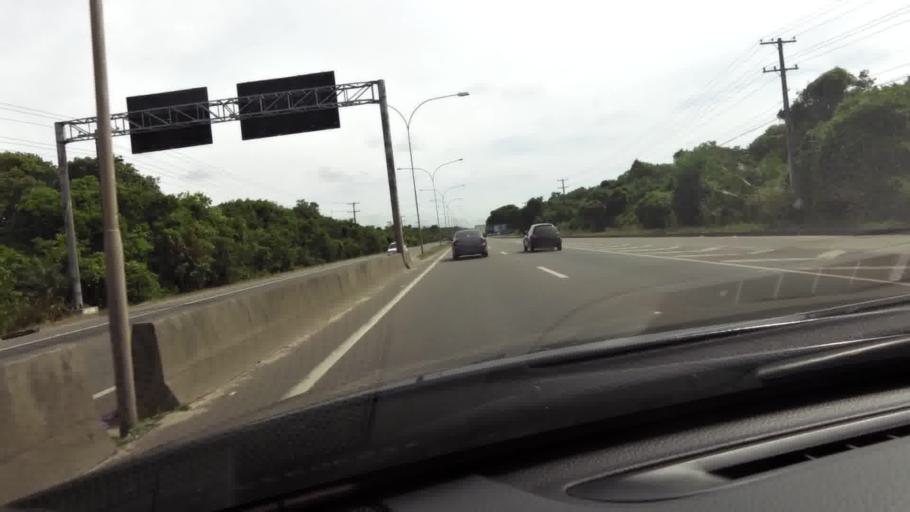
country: BR
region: Espirito Santo
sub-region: Vila Velha
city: Vila Velha
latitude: -20.4129
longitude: -40.3276
